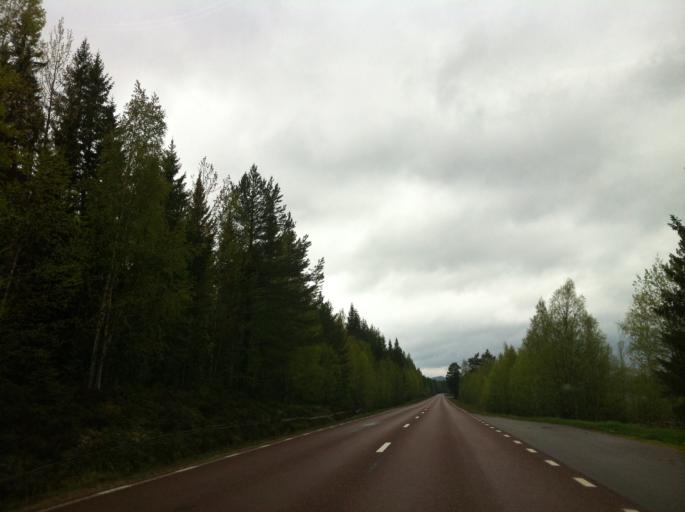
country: SE
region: Jaemtland
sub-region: Harjedalens Kommun
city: Sveg
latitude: 61.9251
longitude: 14.6080
